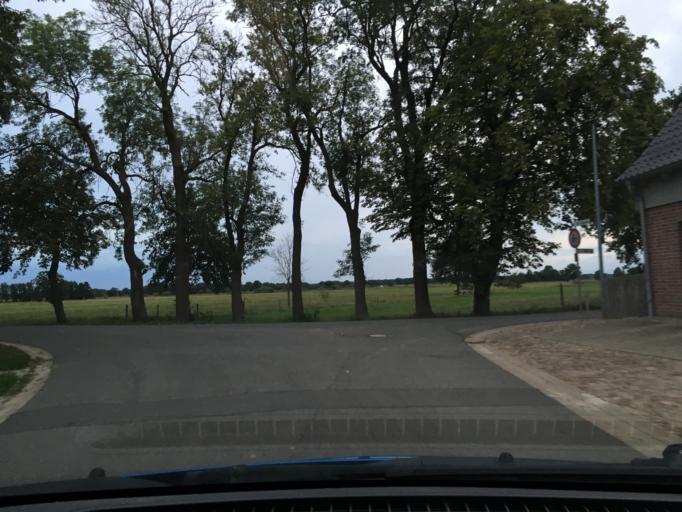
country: DE
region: Lower Saxony
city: Brietlingen
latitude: 53.3501
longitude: 10.4547
